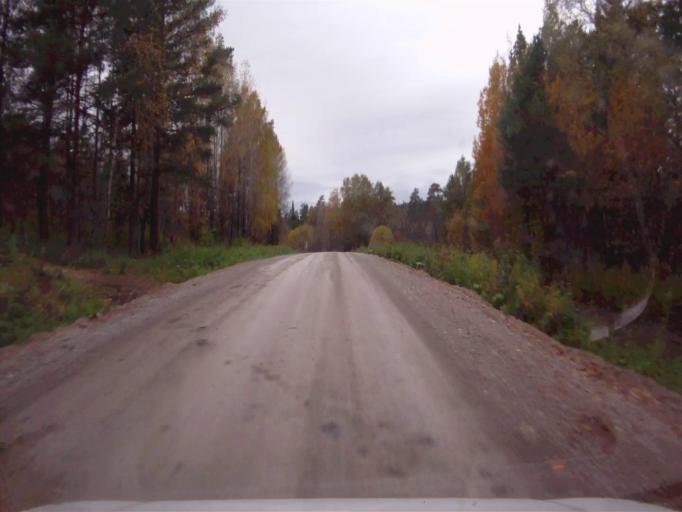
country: RU
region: Chelyabinsk
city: Nyazepetrovsk
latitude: 56.0490
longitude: 59.4989
